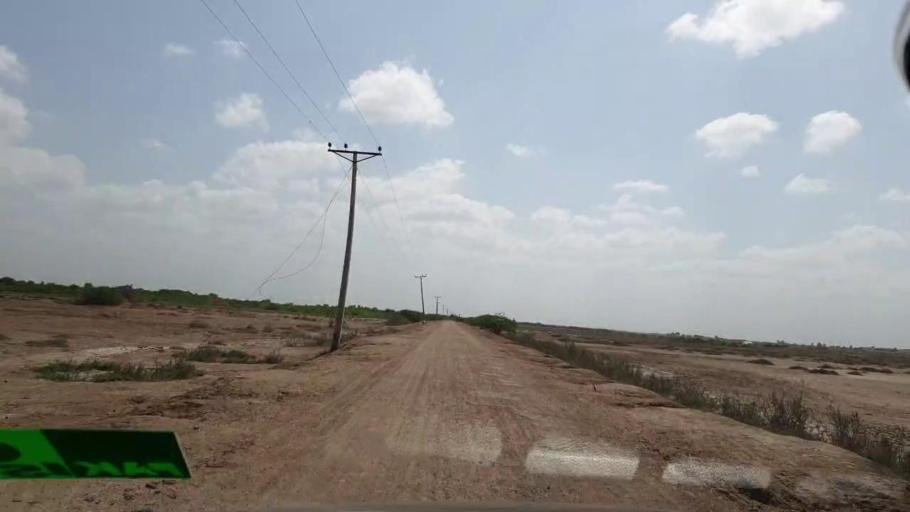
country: PK
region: Sindh
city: Kadhan
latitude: 24.6054
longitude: 69.1852
